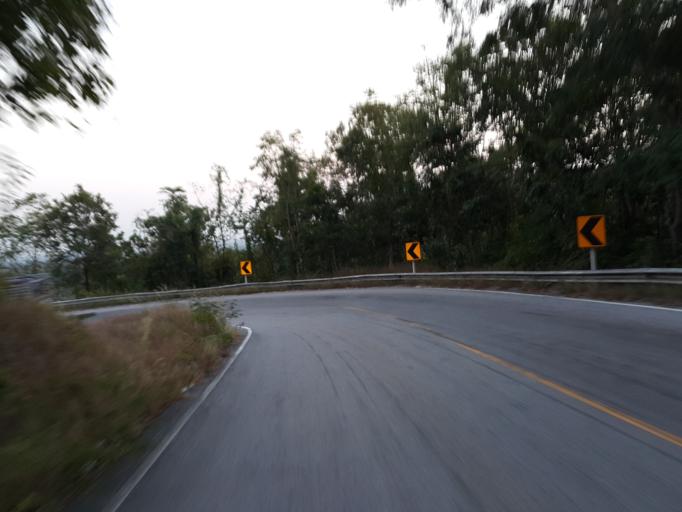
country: TH
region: Lampang
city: Thoen
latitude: 17.6515
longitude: 99.1229
